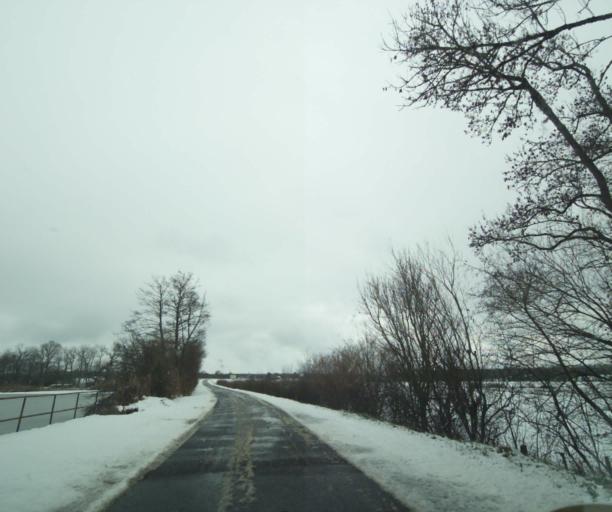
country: FR
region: Champagne-Ardenne
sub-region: Departement de la Haute-Marne
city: Montier-en-Der
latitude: 48.4204
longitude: 4.7299
